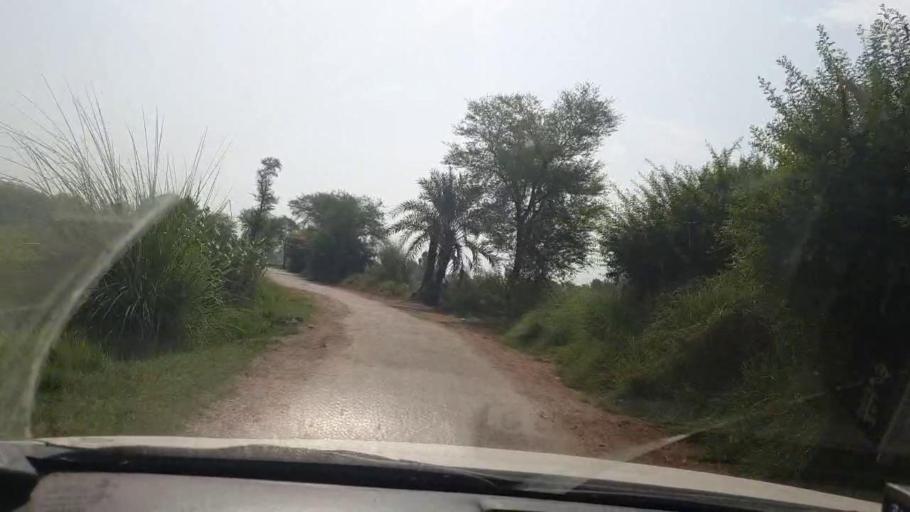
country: PK
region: Sindh
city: Chak
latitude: 27.8253
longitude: 68.7898
